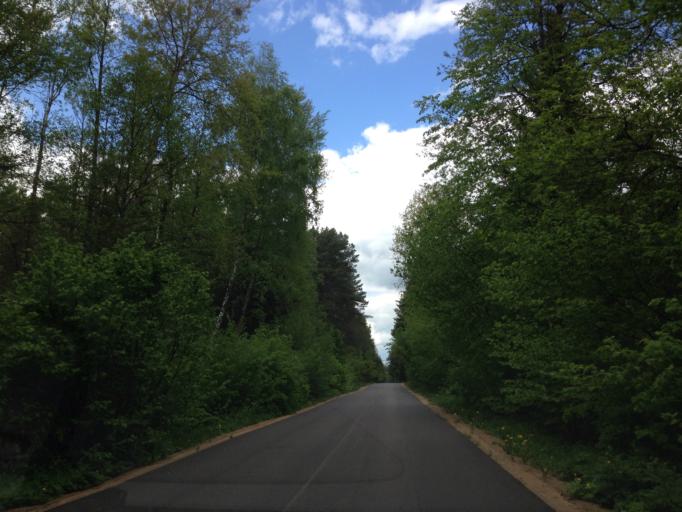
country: PL
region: Podlasie
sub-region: Powiat grajewski
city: Radzilow
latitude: 53.3325
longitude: 22.5996
